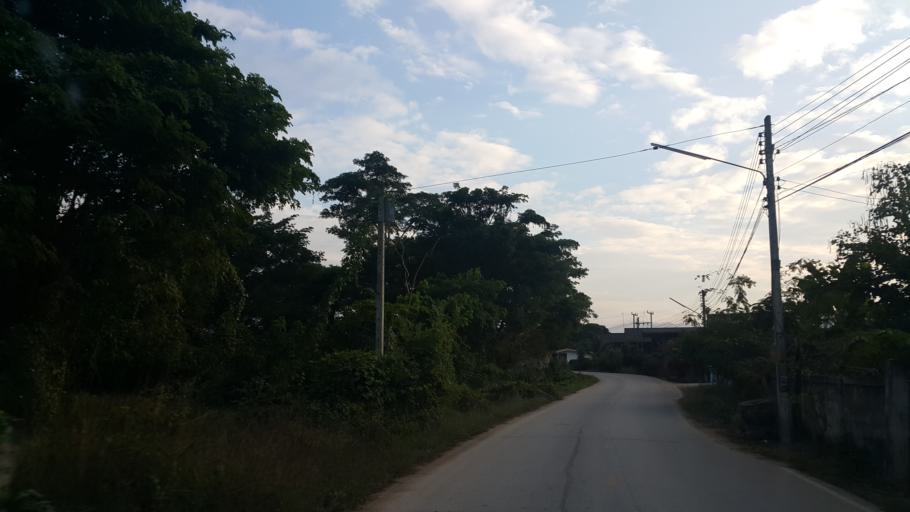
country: TH
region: Lampang
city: Sop Prap
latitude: 17.8997
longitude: 99.3307
